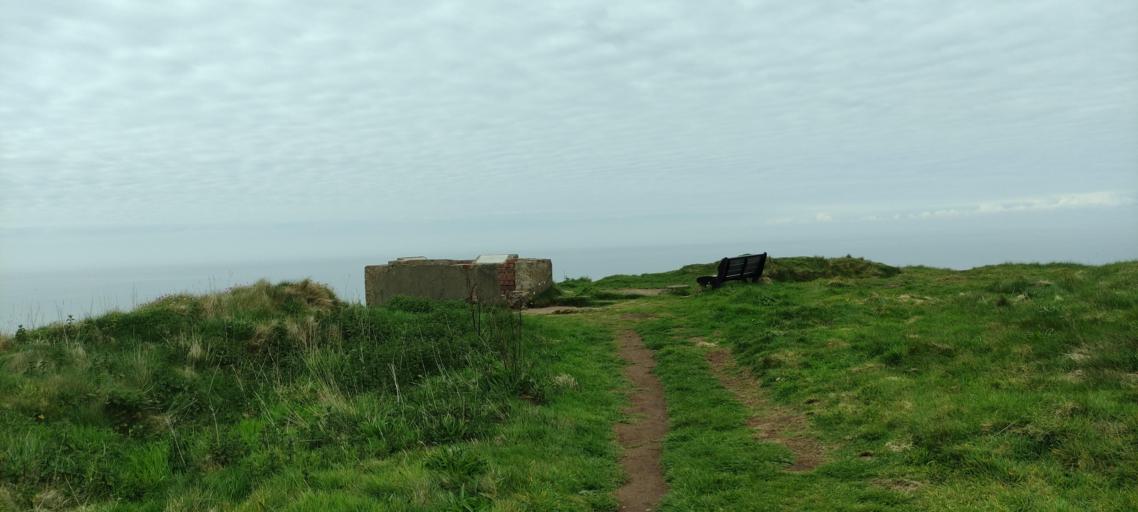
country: GB
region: England
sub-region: Cumbria
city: Saint Bees
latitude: 54.4917
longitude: -3.6188
